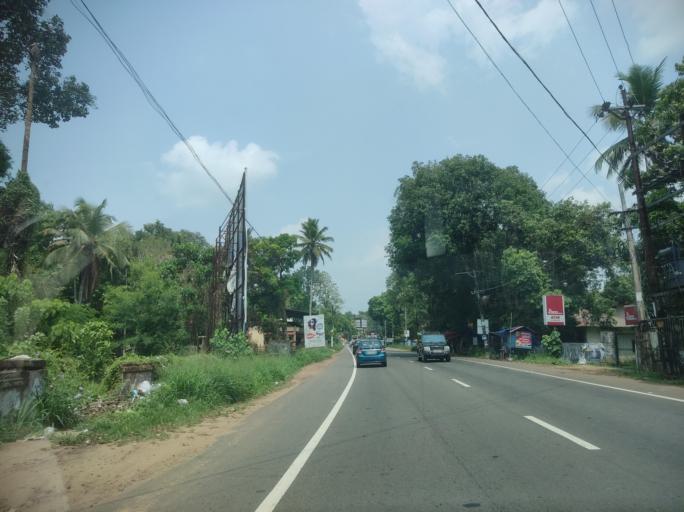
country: IN
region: Kerala
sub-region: Pattanamtitta
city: Tiruvalla
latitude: 9.4092
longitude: 76.5568
